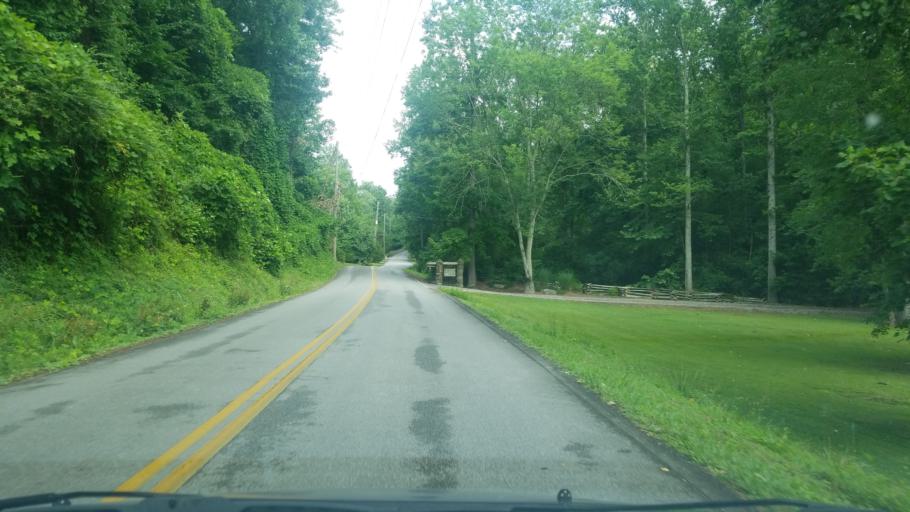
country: US
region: Tennessee
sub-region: Hamilton County
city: Apison
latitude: 35.0134
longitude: -85.0403
